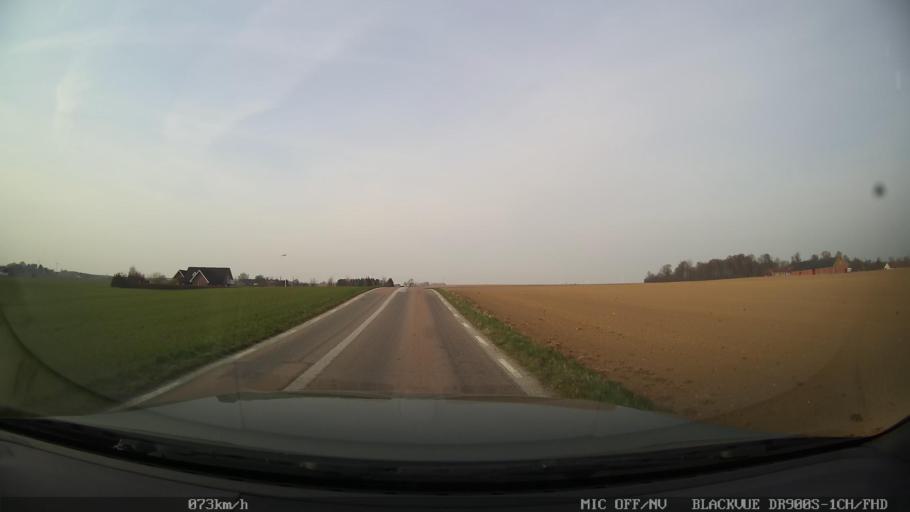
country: SE
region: Skane
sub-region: Ystads Kommun
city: Ystad
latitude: 55.4500
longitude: 13.8314
